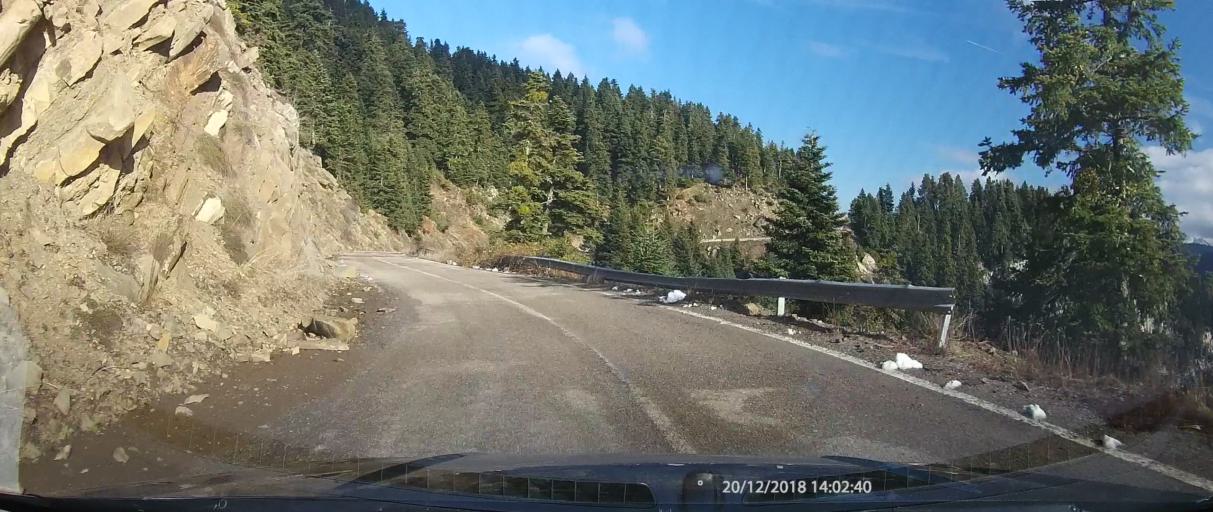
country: GR
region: West Greece
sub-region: Nomos Aitolias kai Akarnanias
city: Thermo
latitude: 38.7380
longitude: 21.6378
